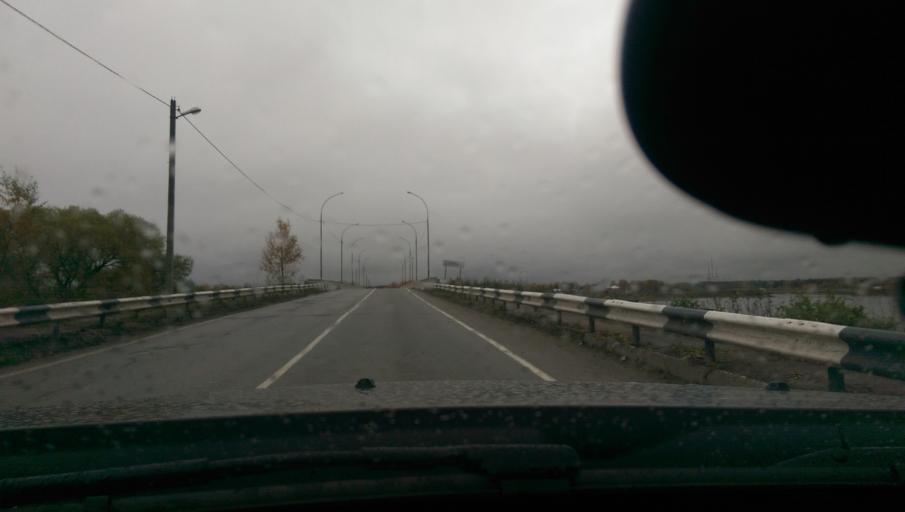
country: RU
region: Jaroslavl
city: Poshekhon'ye
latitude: 58.5106
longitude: 39.1194
